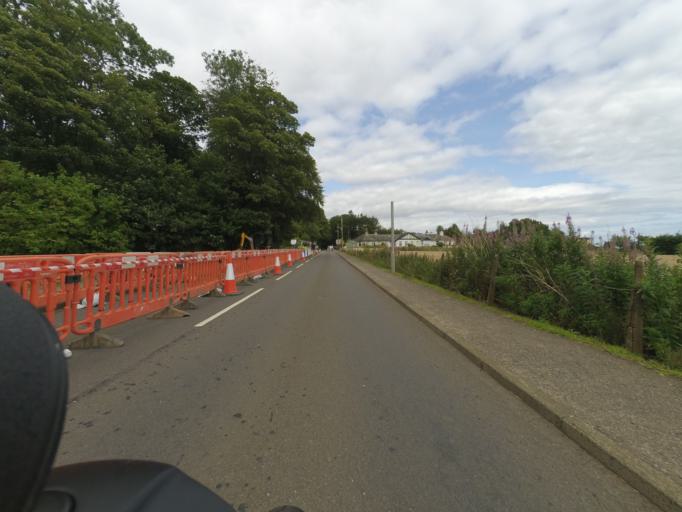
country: GB
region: Scotland
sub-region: Angus
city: Montrose
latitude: 56.7450
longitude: -2.4722
